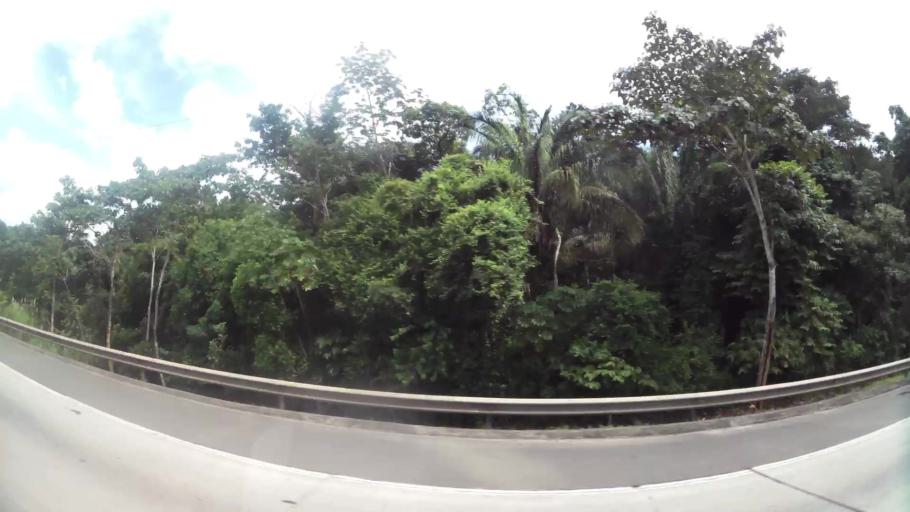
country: PA
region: Panama
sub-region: Distrito Arraijan
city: Arraijan
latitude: 8.9809
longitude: -79.6472
